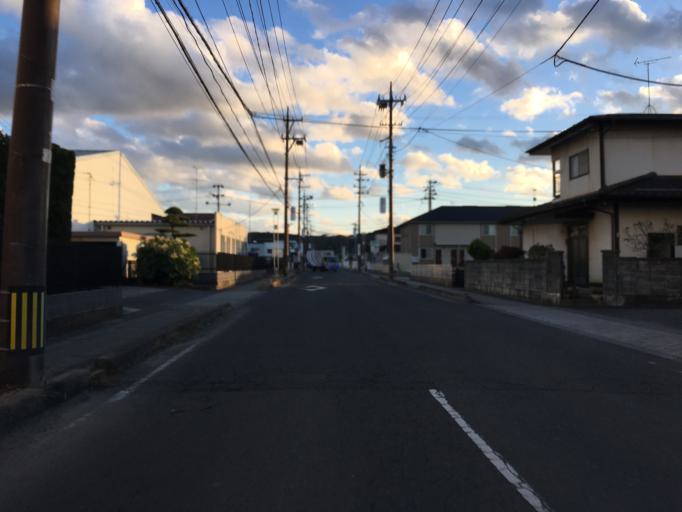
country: JP
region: Fukushima
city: Hobaramachi
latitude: 37.8117
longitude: 140.5517
